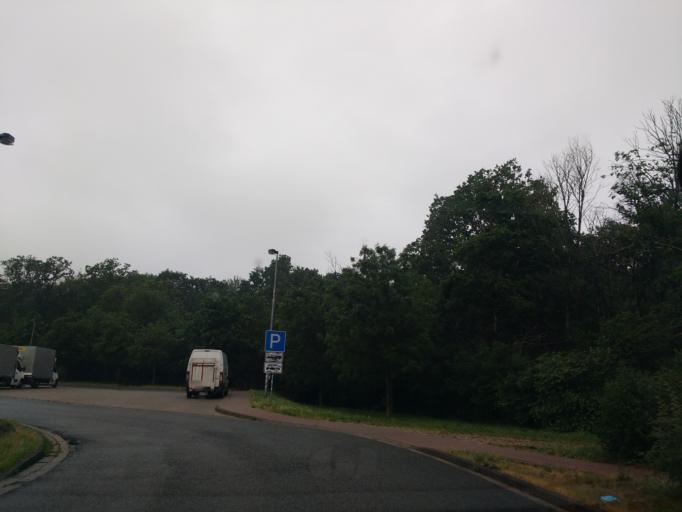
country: DE
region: Lower Saxony
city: Wendeburg
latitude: 52.3407
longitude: 10.3542
